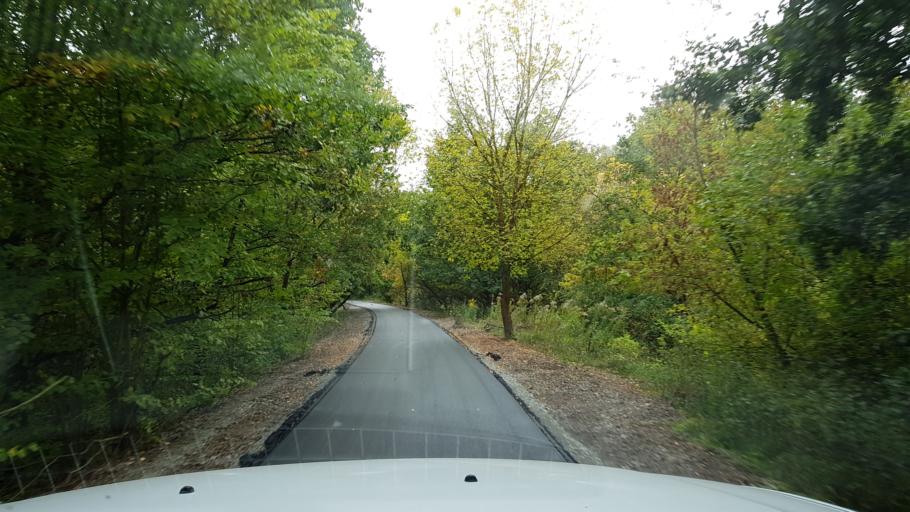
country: PL
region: West Pomeranian Voivodeship
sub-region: Powiat gryfinski
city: Cedynia
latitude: 52.8274
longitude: 14.2405
